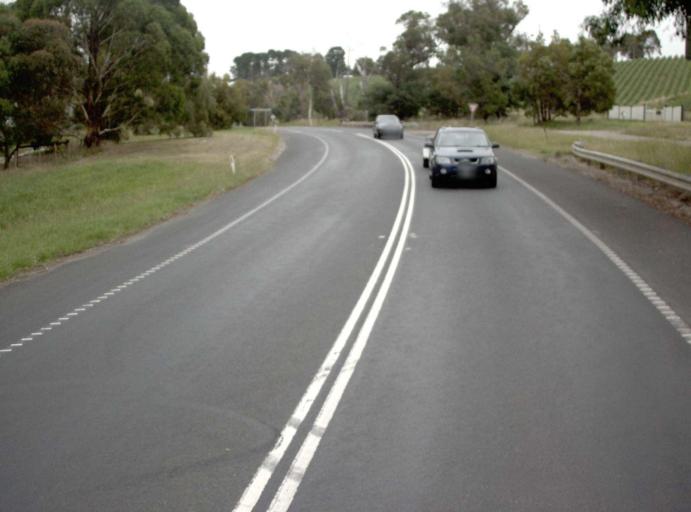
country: AU
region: Victoria
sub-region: Yarra Ranges
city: Yarra Glen
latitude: -37.5827
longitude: 145.4108
